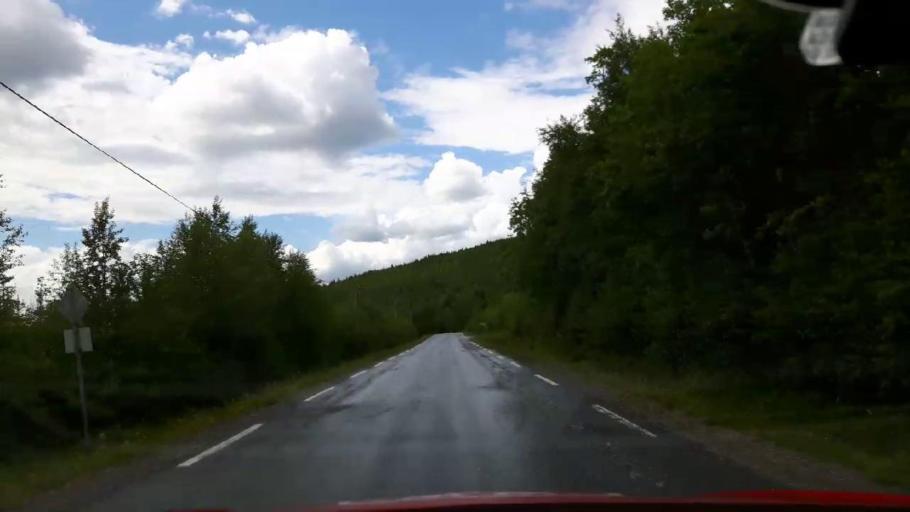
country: NO
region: Nord-Trondelag
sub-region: Lierne
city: Sandvika
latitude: 64.1169
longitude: 13.9639
